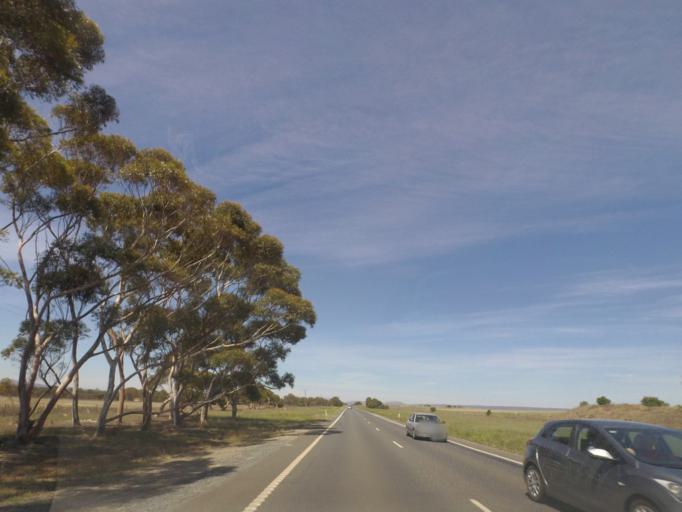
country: AU
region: Victoria
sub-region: Moorabool
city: Bacchus Marsh
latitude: -37.7840
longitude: 144.4274
